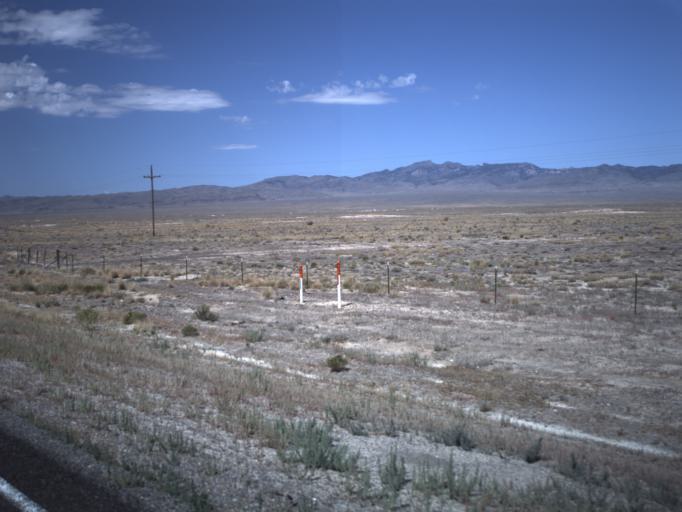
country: US
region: Utah
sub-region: Millard County
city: Delta
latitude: 39.1204
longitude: -113.1203
